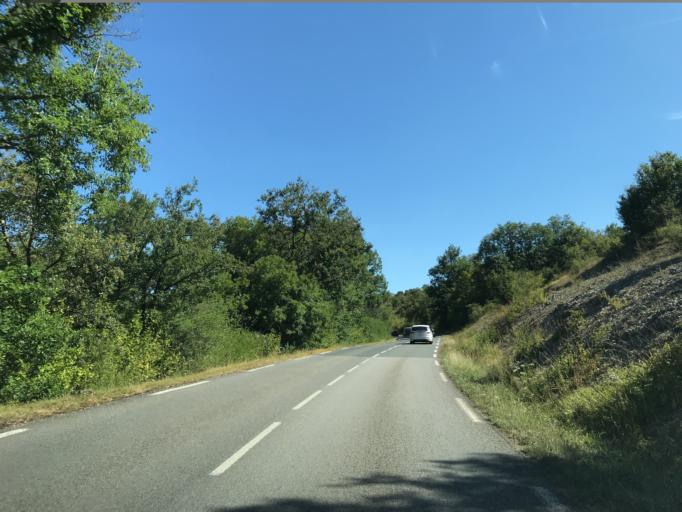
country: FR
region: Limousin
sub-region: Departement de la Correze
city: Larche
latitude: 45.0368
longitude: 1.3753
